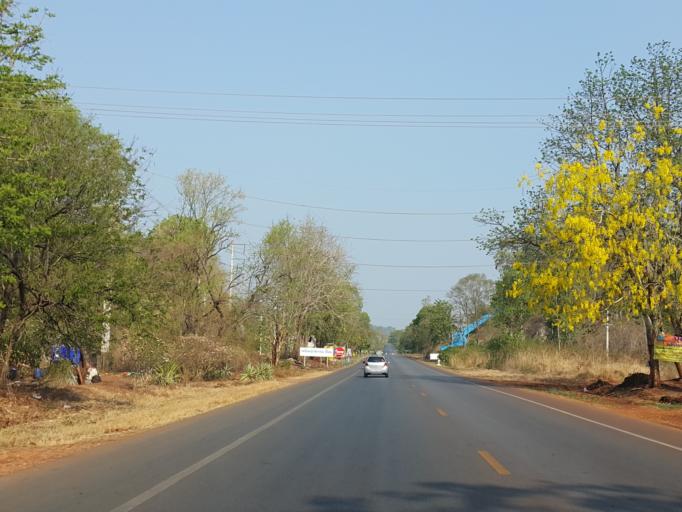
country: TH
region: Kanchanaburi
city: Sai Yok
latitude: 14.1013
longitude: 99.2289
